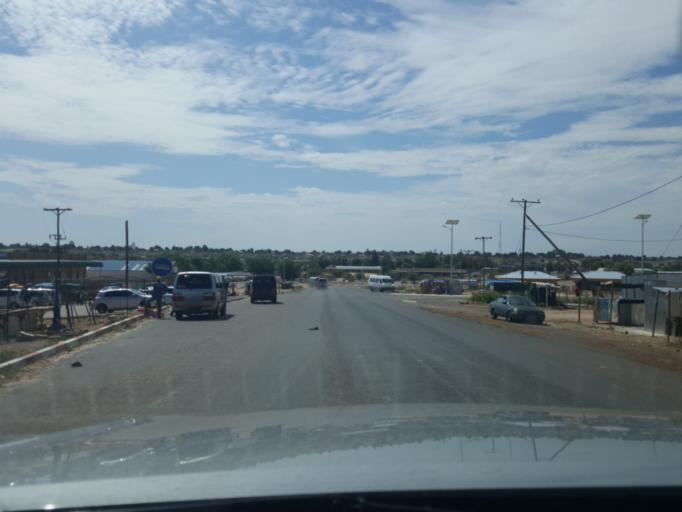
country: BW
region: Kweneng
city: Letlhakeng
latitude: -24.1020
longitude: 25.0305
